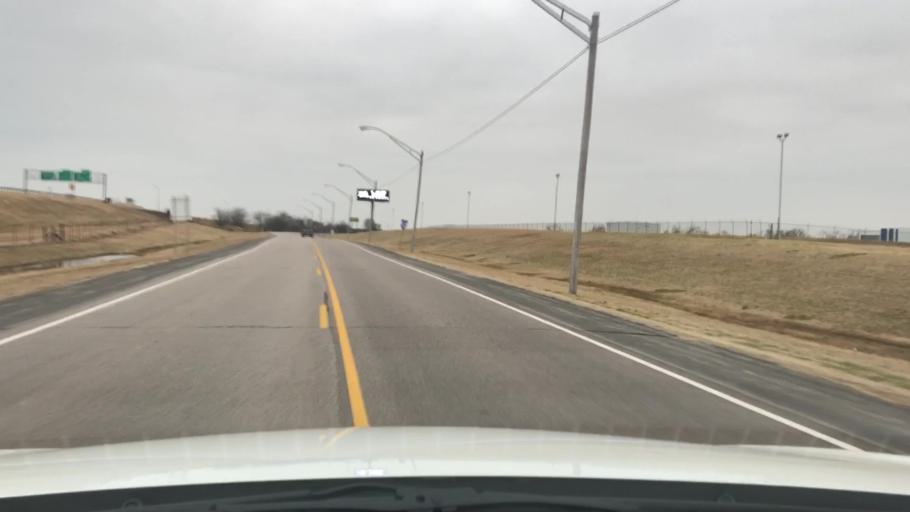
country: US
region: Oklahoma
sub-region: Carter County
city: Ardmore
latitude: 34.1800
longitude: -97.1690
